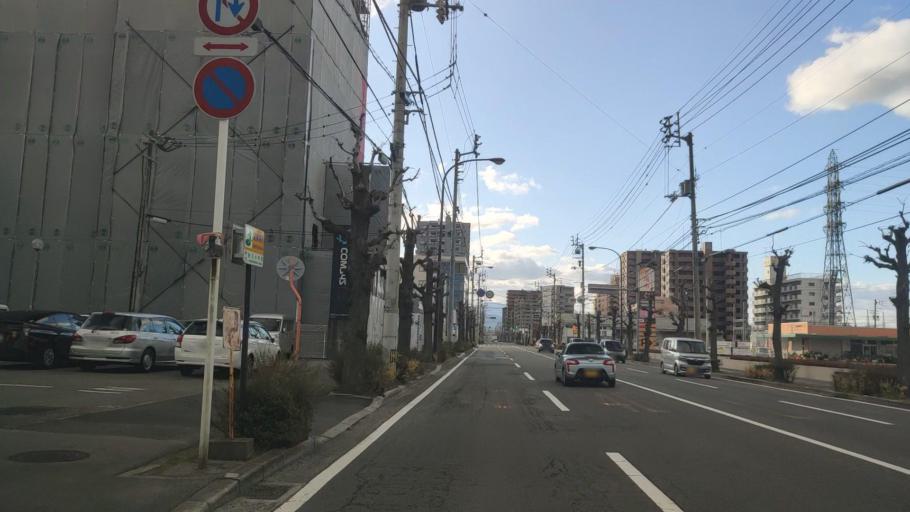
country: JP
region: Ehime
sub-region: Shikoku-chuo Shi
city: Matsuyama
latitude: 33.8367
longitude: 132.7525
